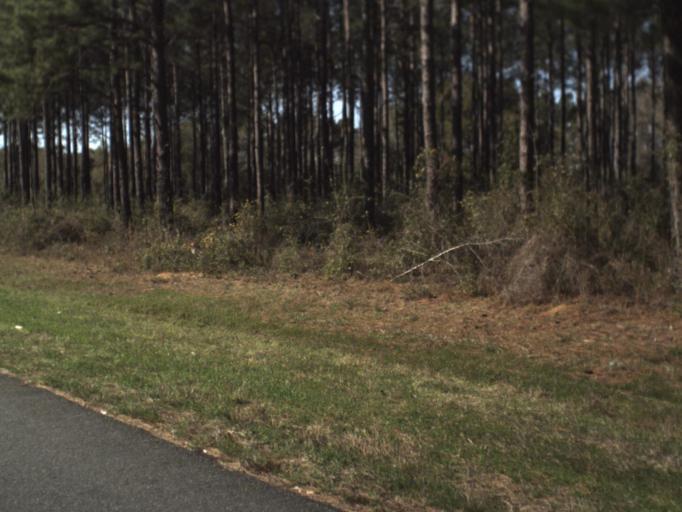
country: US
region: Florida
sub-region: Gulf County
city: Wewahitchka
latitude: 30.2356
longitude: -85.2110
